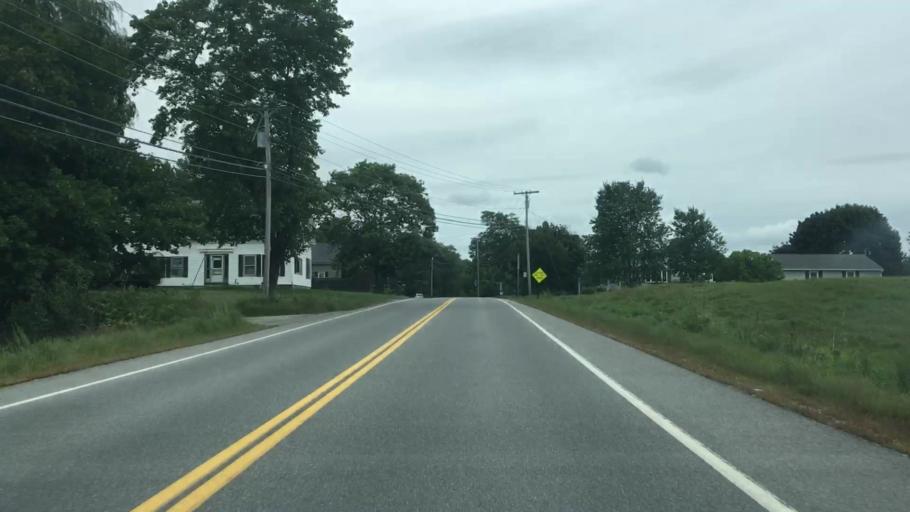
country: US
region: Maine
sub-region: Cumberland County
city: Yarmouth
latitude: 43.8282
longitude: -70.1956
